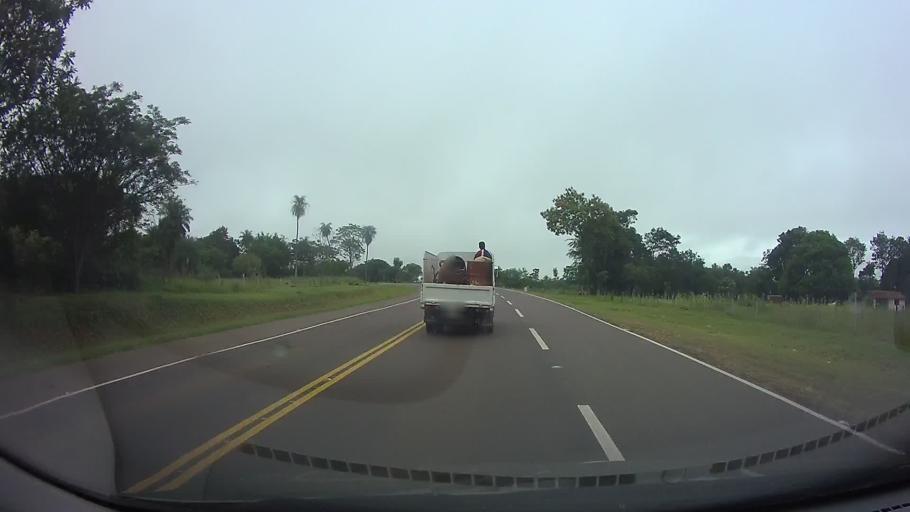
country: PY
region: Paraguari
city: Paraguari
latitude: -25.6093
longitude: -57.1852
